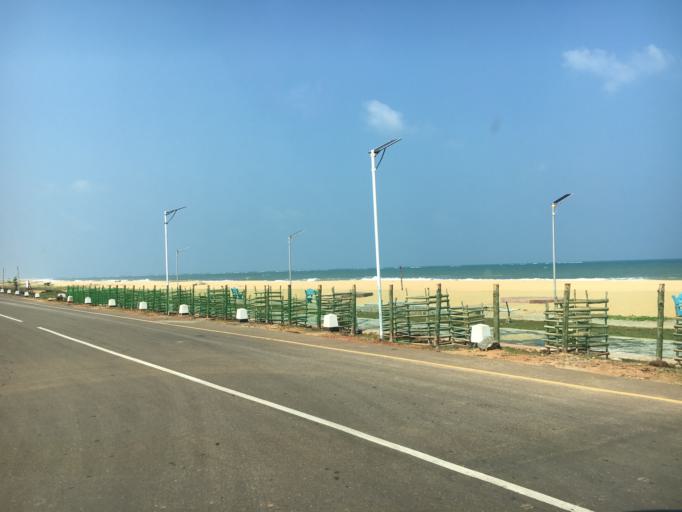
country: LK
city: Padaviya Divisional Secretariat
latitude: 9.2717
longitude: 80.8190
